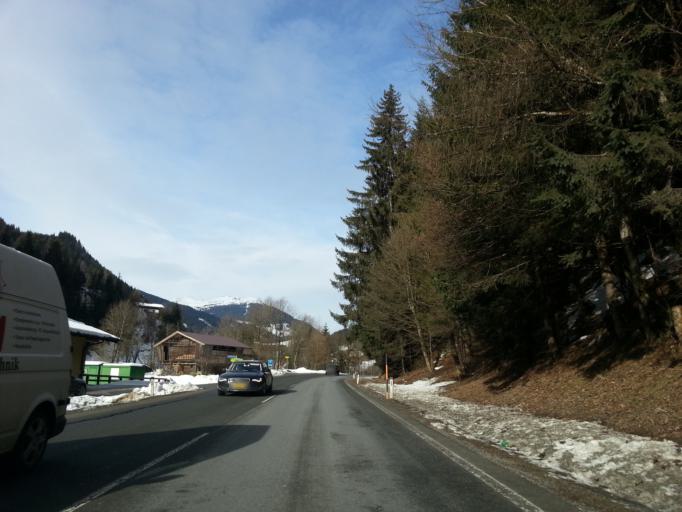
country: AT
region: Salzburg
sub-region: Politischer Bezirk Zell am See
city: Viehhofen
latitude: 47.3655
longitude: 12.7461
